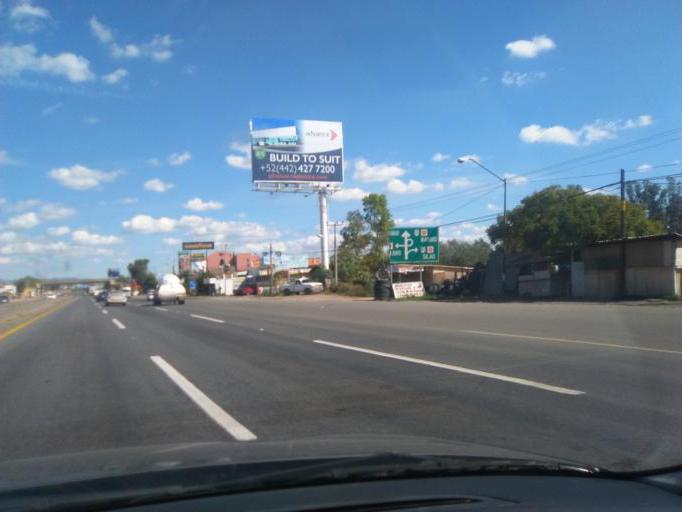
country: MX
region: Guanajuato
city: Silao
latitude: 20.9550
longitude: -101.4213
